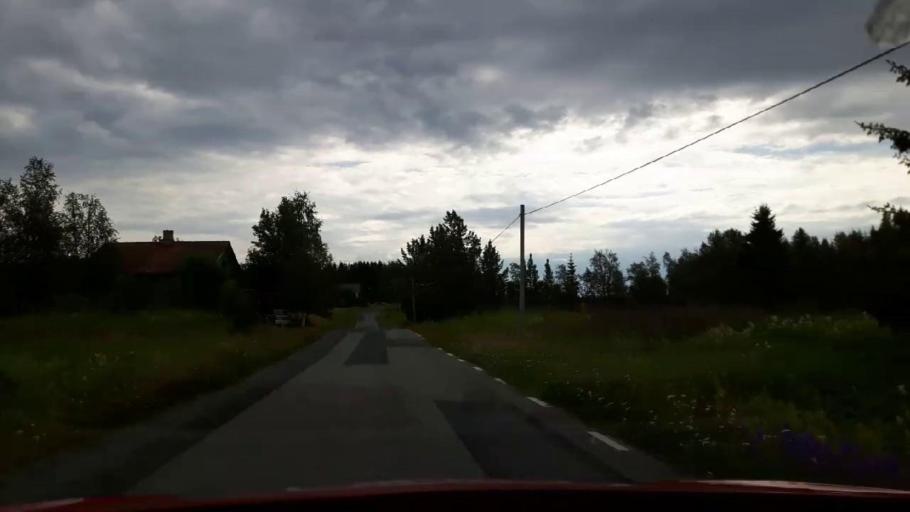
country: SE
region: Jaemtland
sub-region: OEstersunds Kommun
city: Lit
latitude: 63.3730
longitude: 15.1168
